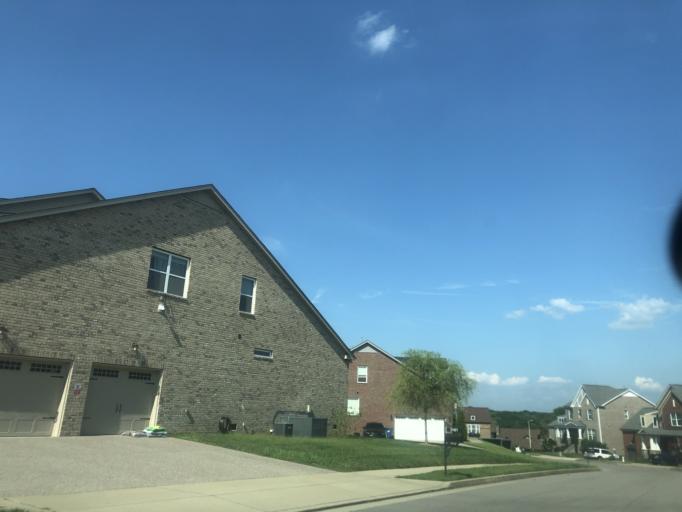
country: US
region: Tennessee
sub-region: Wilson County
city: Green Hill
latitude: 36.1429
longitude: -86.5908
